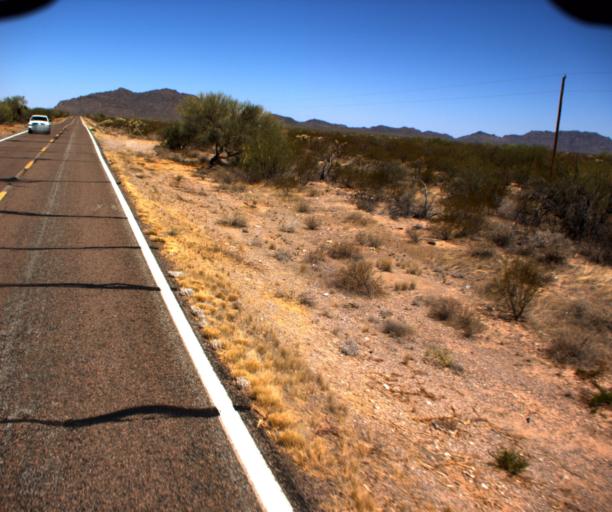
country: US
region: Arizona
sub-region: Pima County
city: Ajo
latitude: 32.2152
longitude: -112.6392
